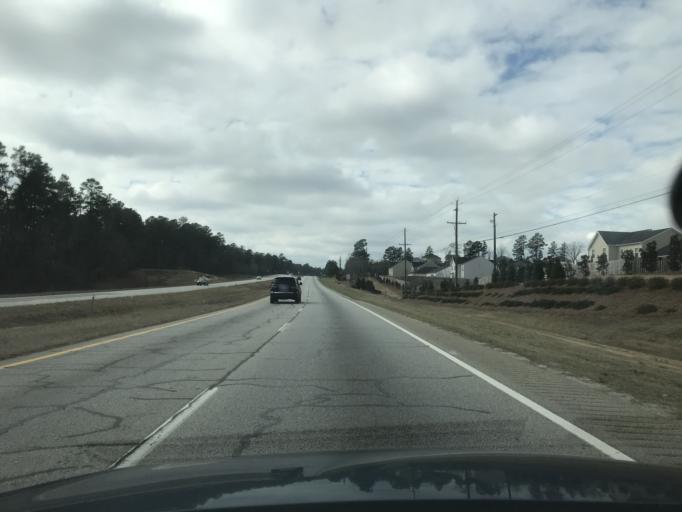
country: US
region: Georgia
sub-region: Columbia County
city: Grovetown
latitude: 33.4386
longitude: -82.1418
